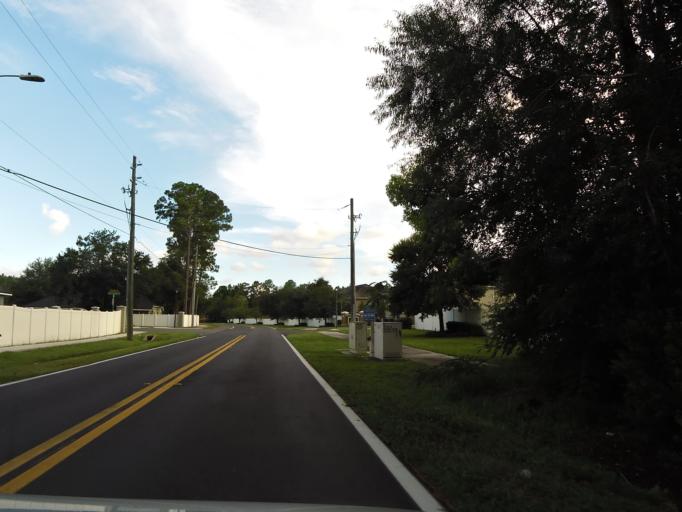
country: US
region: Florida
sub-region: Duval County
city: Jacksonville
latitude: 30.4353
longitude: -81.6932
